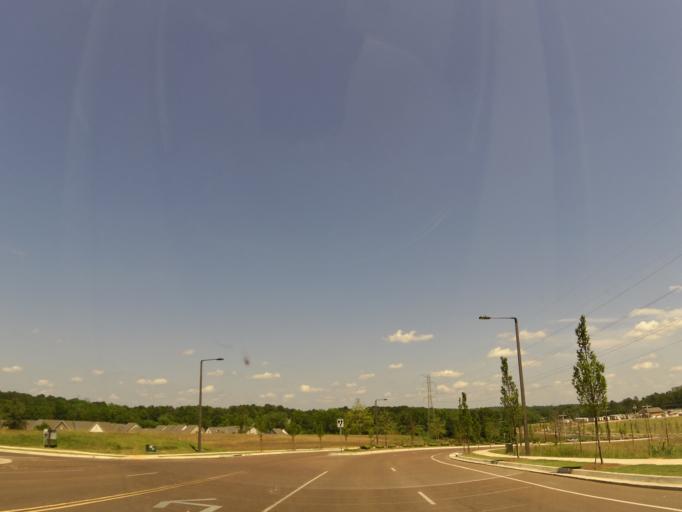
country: US
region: Mississippi
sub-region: Lafayette County
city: University
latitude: 34.3511
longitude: -89.5324
